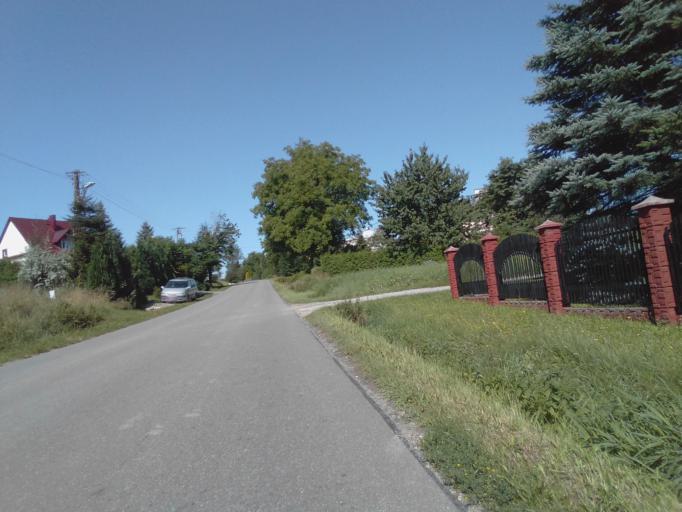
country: PL
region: Subcarpathian Voivodeship
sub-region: Powiat krosnienski
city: Dukla
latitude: 49.5994
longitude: 21.6941
